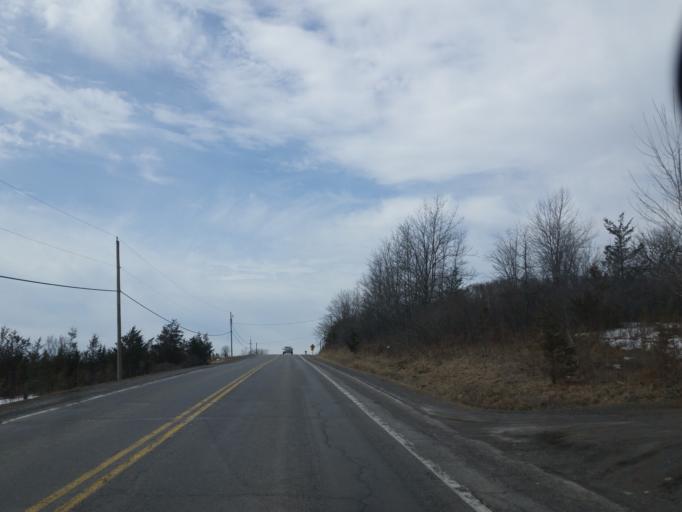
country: CA
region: Ontario
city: Deseronto
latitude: 44.1942
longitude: -77.1927
